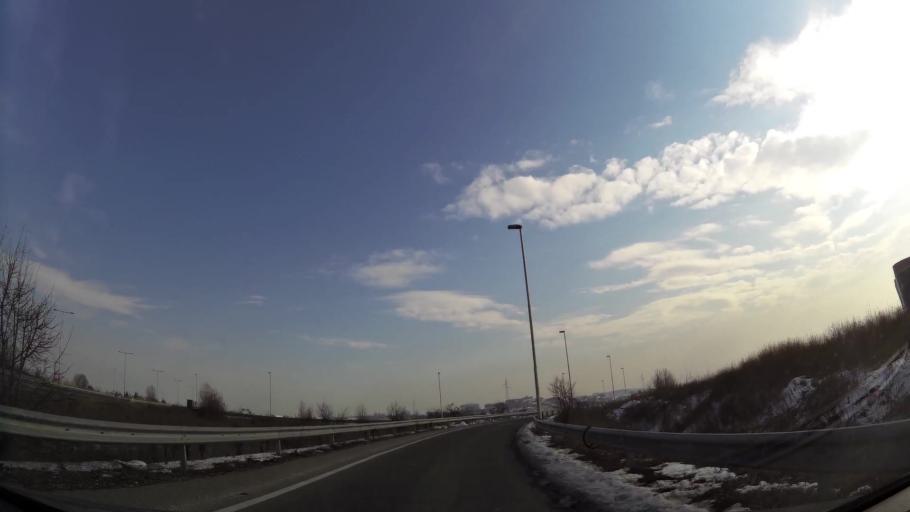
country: MK
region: Suto Orizari
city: Suto Orizare
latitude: 42.0526
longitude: 21.4202
